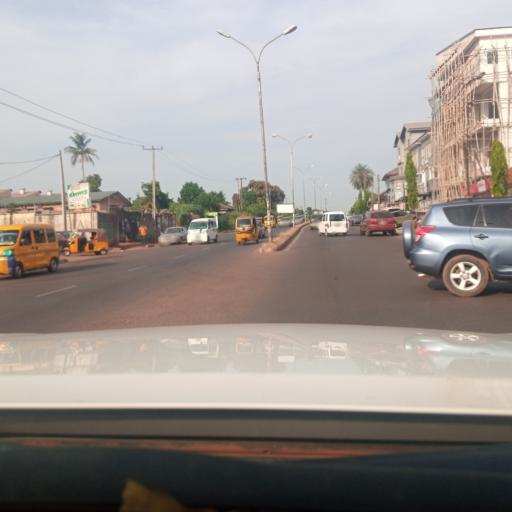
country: NG
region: Enugu
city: Enugu
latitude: 6.4472
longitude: 7.4995
